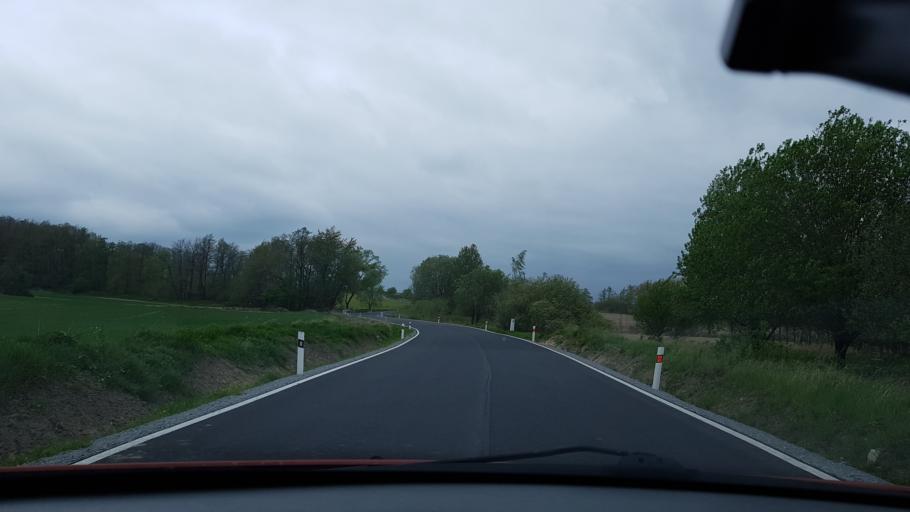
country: PL
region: Opole Voivodeship
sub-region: Powiat nyski
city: Kamienica
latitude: 50.4313
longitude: 16.9516
